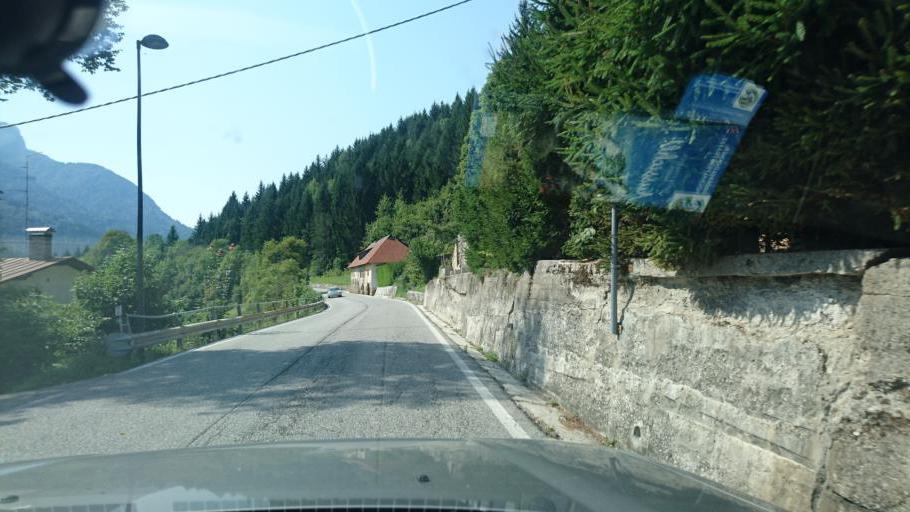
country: IT
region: Friuli Venezia Giulia
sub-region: Provincia di Udine
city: Tarvisio
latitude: 46.5024
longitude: 13.5890
